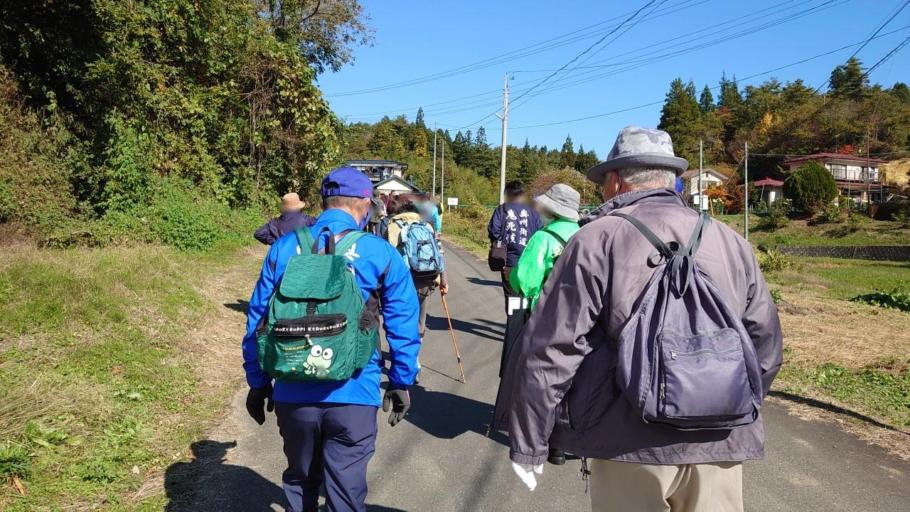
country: JP
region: Iwate
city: Ichinoseki
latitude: 38.8701
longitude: 141.1273
